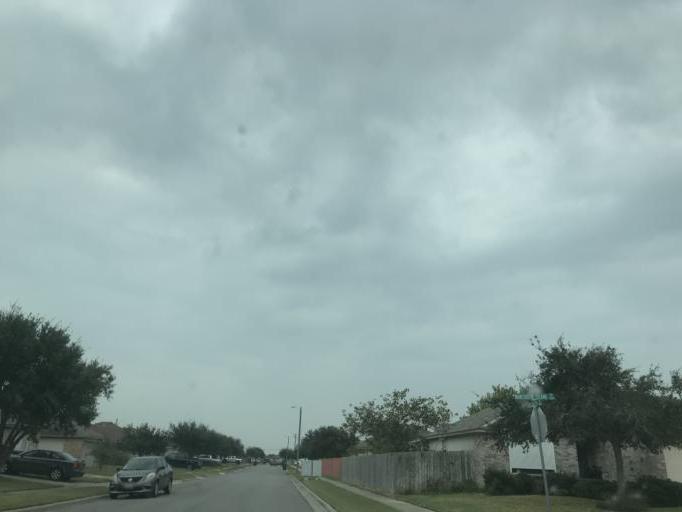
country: US
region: Texas
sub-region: Nueces County
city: Corpus Christi
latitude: 27.6680
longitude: -97.3409
